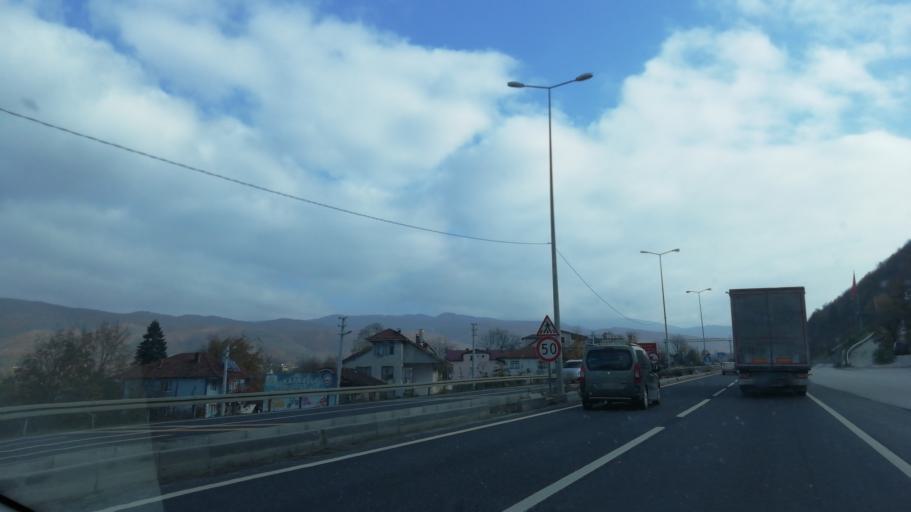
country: TR
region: Duzce
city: Kaynasli
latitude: 40.7724
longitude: 31.3308
